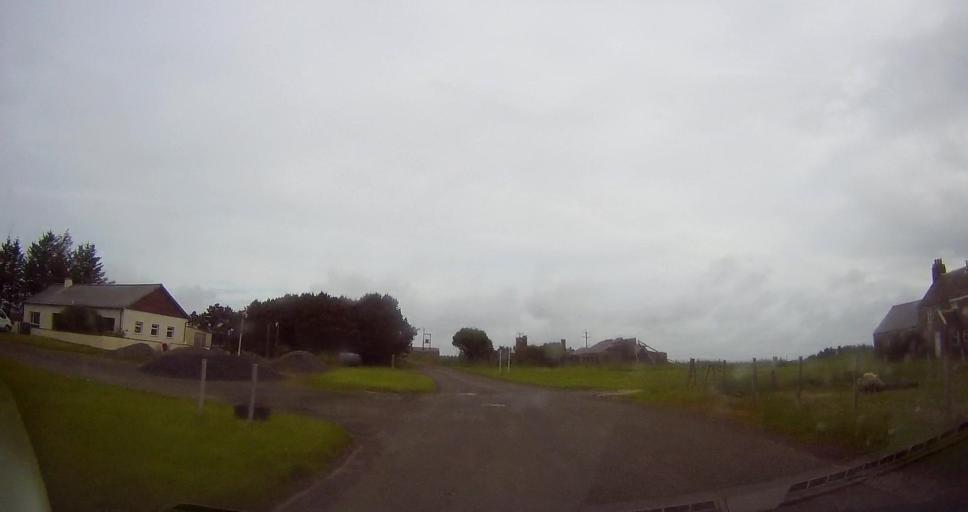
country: GB
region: Scotland
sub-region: Orkney Islands
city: Stromness
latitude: 58.8317
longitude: -3.2067
